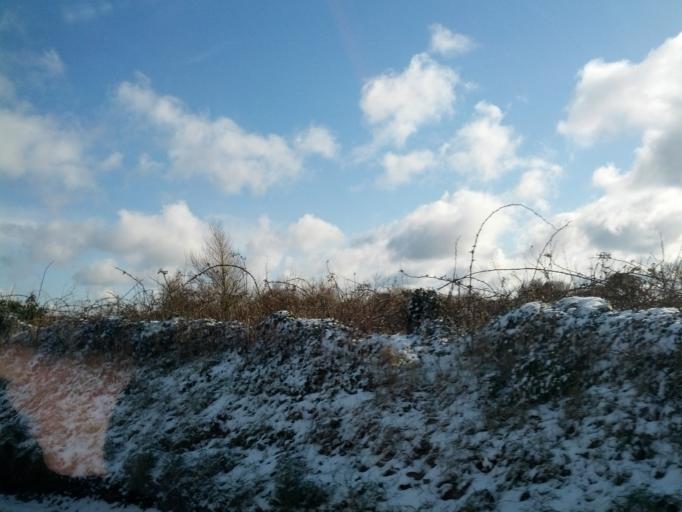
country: IE
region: Connaught
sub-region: County Galway
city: Gort
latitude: 53.1499
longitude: -8.8856
